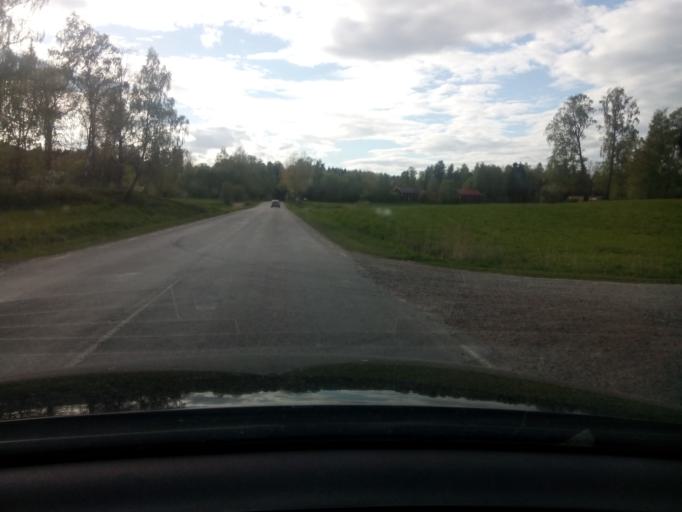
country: SE
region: Soedermanland
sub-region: Nykopings Kommun
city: Stigtomta
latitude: 58.9533
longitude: 16.8624
